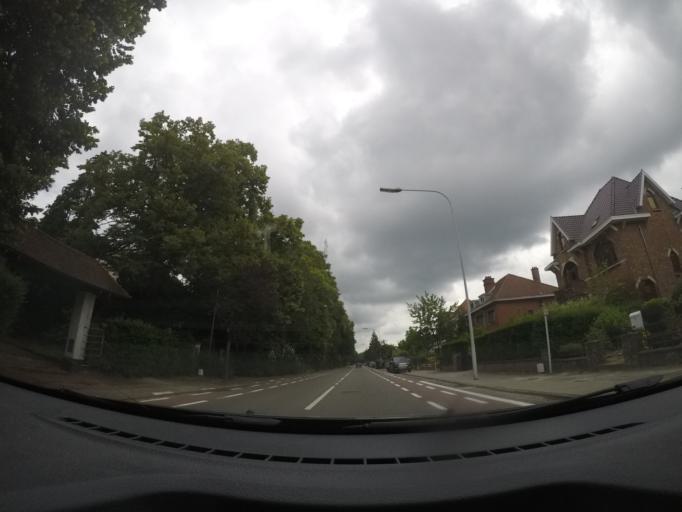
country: BE
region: Flanders
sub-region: Provincie Vlaams-Brabant
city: Sint-Genesius-Rode
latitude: 50.7502
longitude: 4.3663
